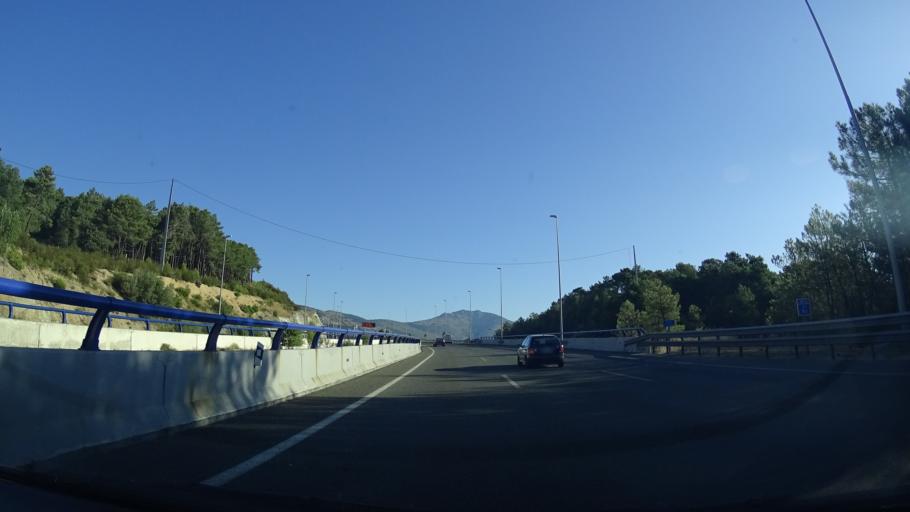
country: ES
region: Madrid
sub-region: Provincia de Madrid
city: Guadarrama
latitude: 40.6819
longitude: -4.1177
